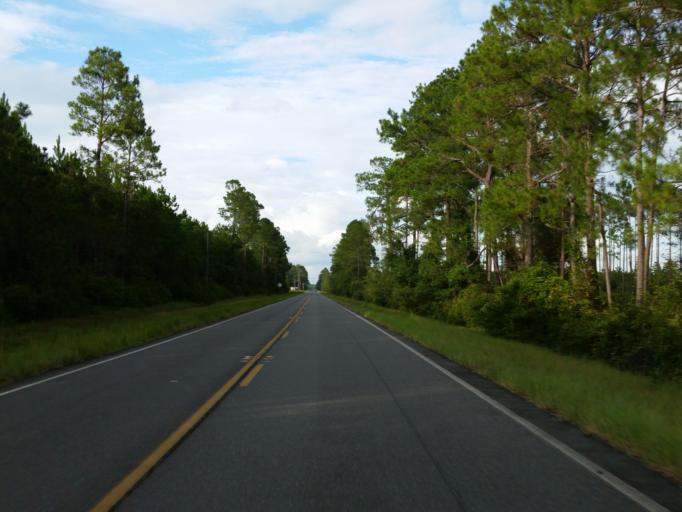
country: US
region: Florida
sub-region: Hamilton County
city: Jasper
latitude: 30.6400
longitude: -82.5793
